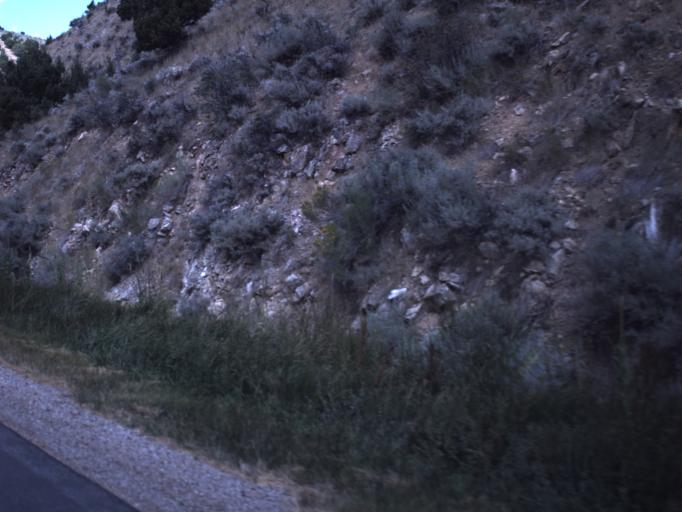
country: US
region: Utah
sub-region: Rich County
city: Randolph
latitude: 41.8230
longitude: -111.2919
